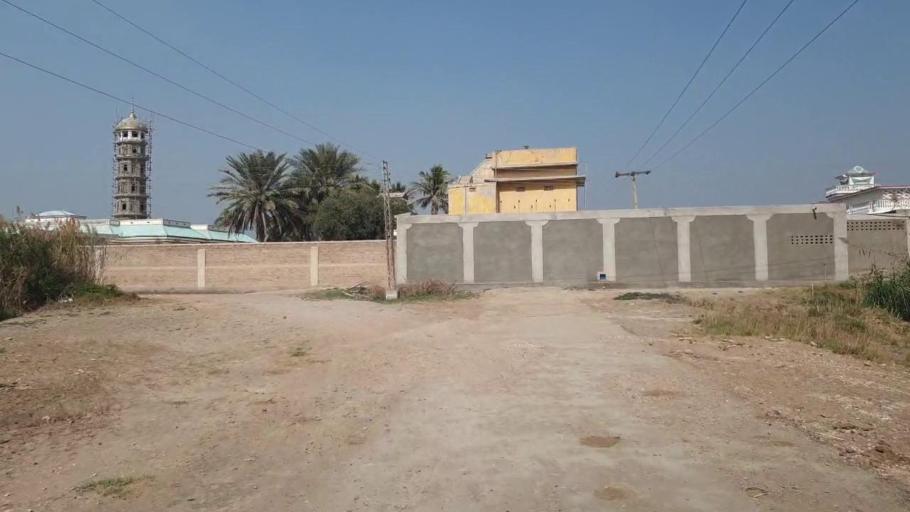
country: PK
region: Sindh
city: Chambar
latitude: 25.3736
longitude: 68.8798
